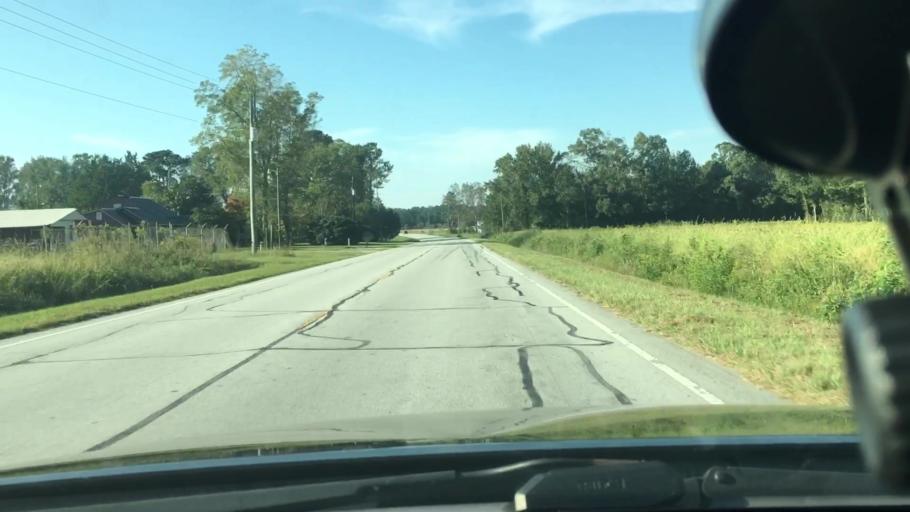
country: US
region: North Carolina
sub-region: Craven County
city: Vanceboro
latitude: 35.3167
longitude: -77.1629
